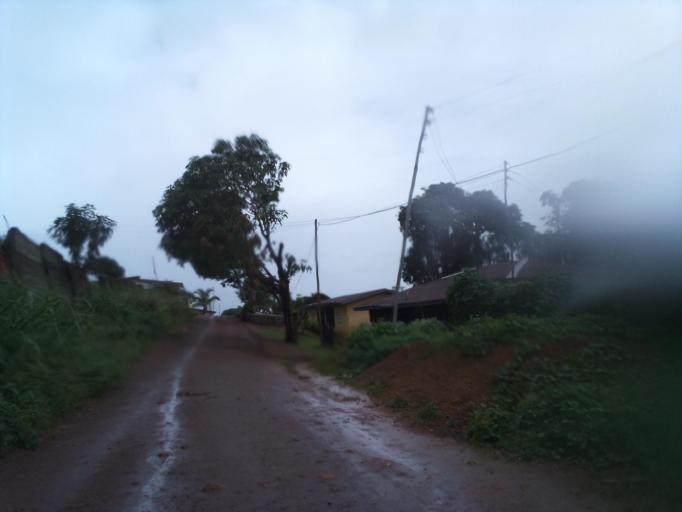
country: SL
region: Eastern Province
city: Kenema
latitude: 7.8541
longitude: -11.1957
